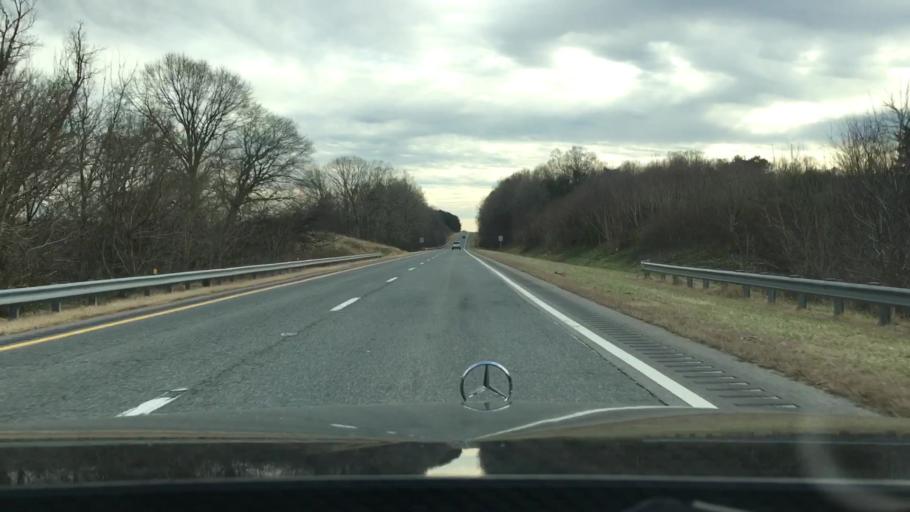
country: US
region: Virginia
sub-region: Pittsylvania County
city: Gretna
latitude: 36.9457
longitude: -79.3782
